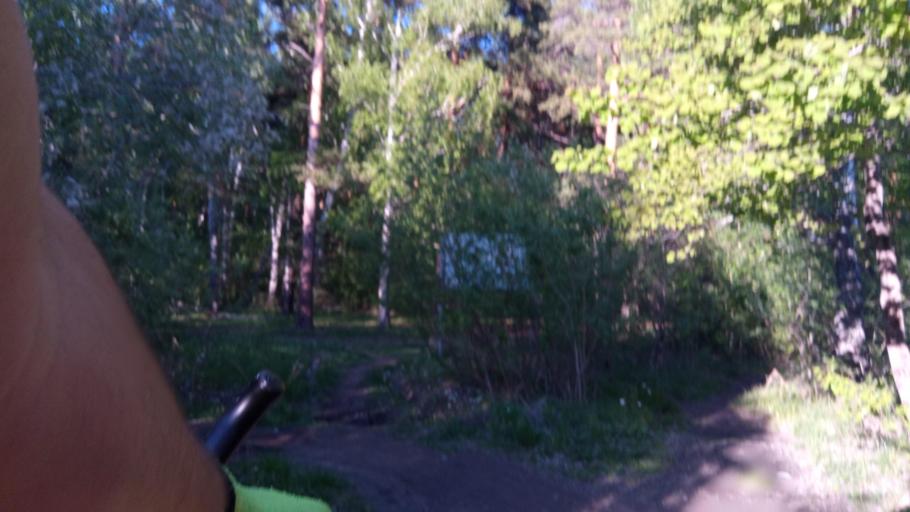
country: RU
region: Chelyabinsk
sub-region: Gorod Chelyabinsk
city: Chelyabinsk
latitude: 55.1405
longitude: 61.3309
